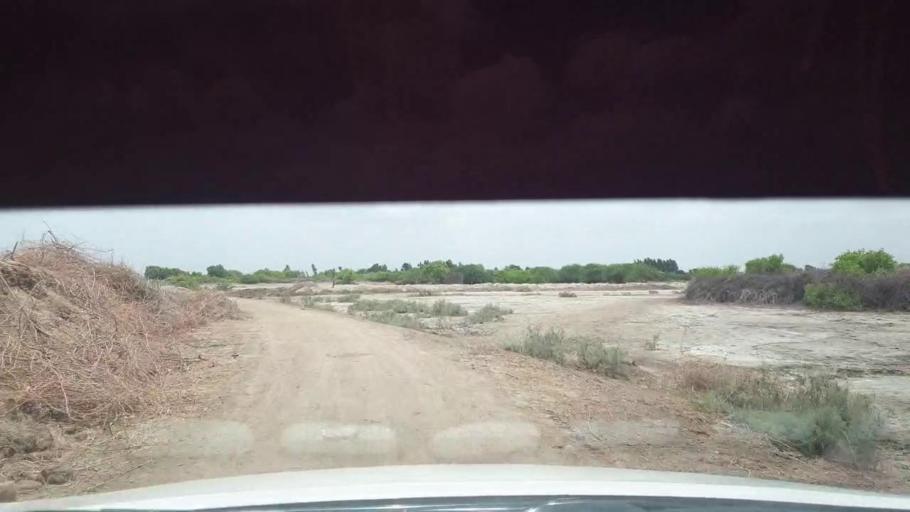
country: PK
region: Sindh
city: Kadhan
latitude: 24.4819
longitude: 69.0001
